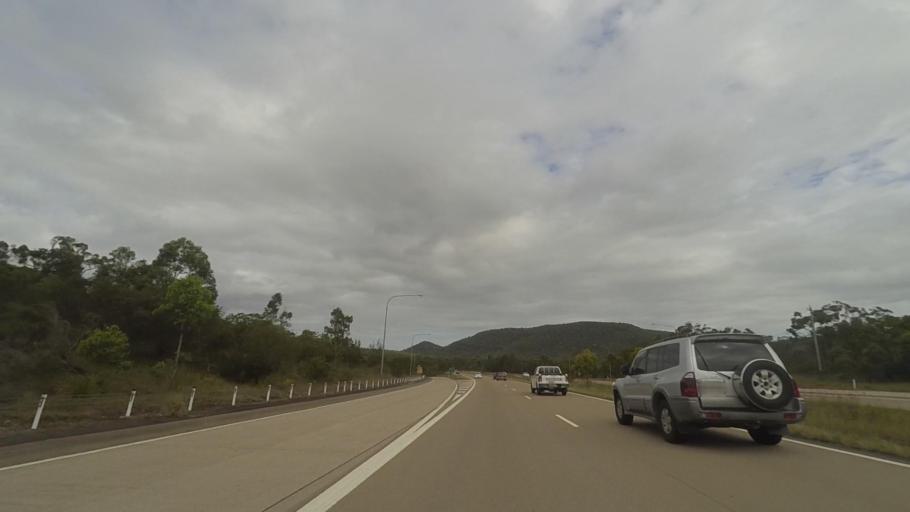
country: AU
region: New South Wales
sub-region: Port Stephens Shire
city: Port Stephens
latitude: -32.6304
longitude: 151.9929
